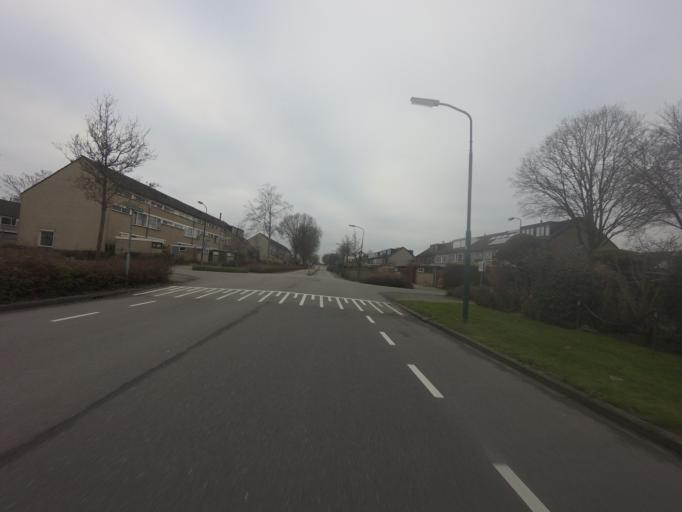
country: NL
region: Utrecht
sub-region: Gemeente Montfoort
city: Montfoort
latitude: 52.0610
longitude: 4.9206
